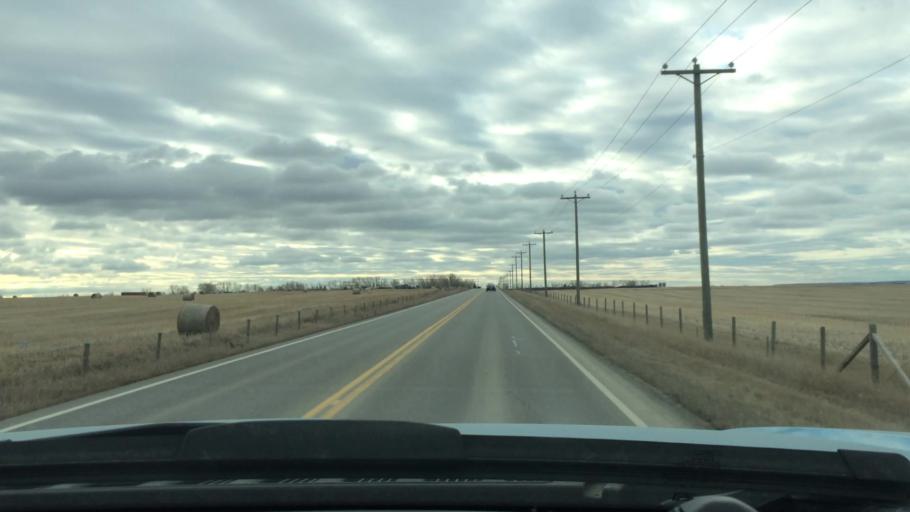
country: CA
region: Alberta
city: Airdrie
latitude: 51.2404
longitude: -114.0250
